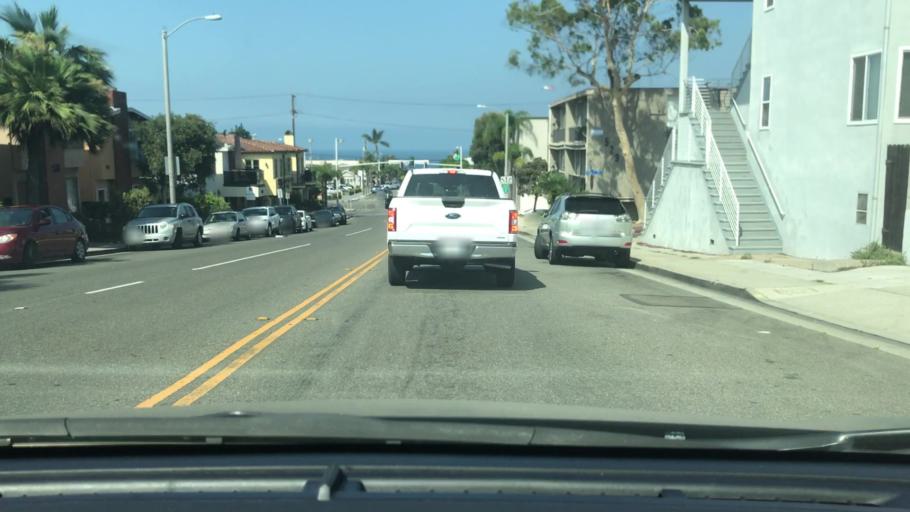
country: US
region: California
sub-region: Los Angeles County
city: Manhattan Beach
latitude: 33.8863
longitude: -118.4064
